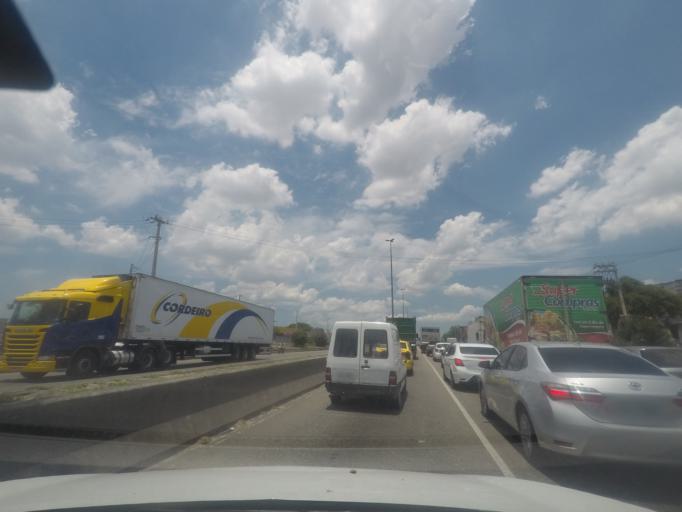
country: BR
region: Rio de Janeiro
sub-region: Sao Joao De Meriti
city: Sao Joao de Meriti
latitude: -22.8267
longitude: -43.3394
